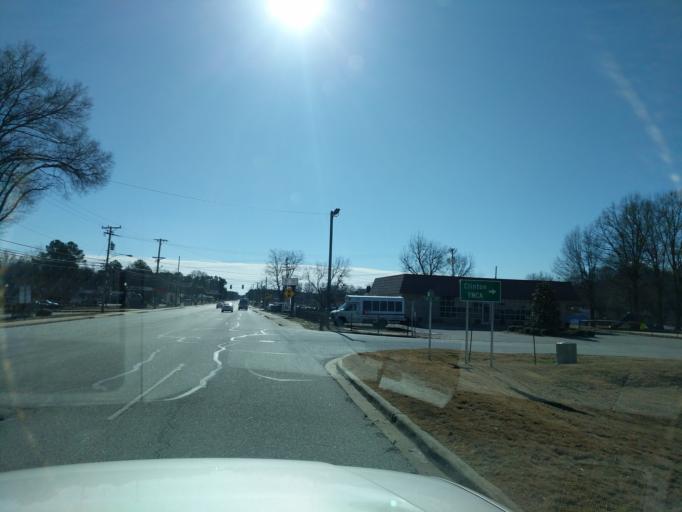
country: US
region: South Carolina
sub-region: Laurens County
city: Clinton
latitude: 34.4555
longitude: -81.8770
